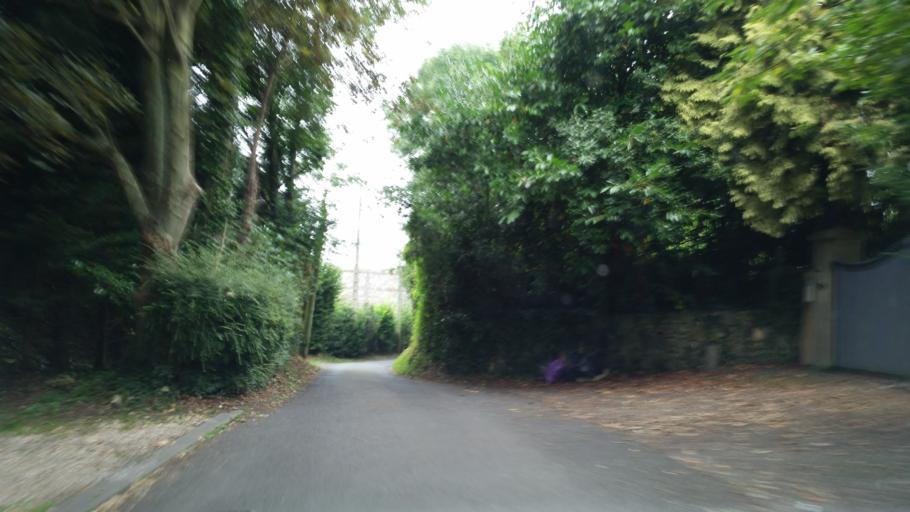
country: FR
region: Lower Normandy
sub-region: Departement du Calvados
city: Honfleur
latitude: 49.4116
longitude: 0.2343
